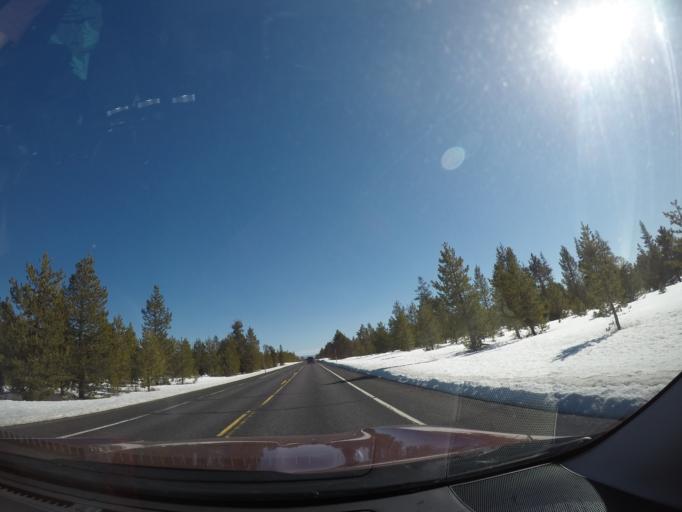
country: US
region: Oregon
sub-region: Deschutes County
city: Three Rivers
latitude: 43.8803
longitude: -121.5668
